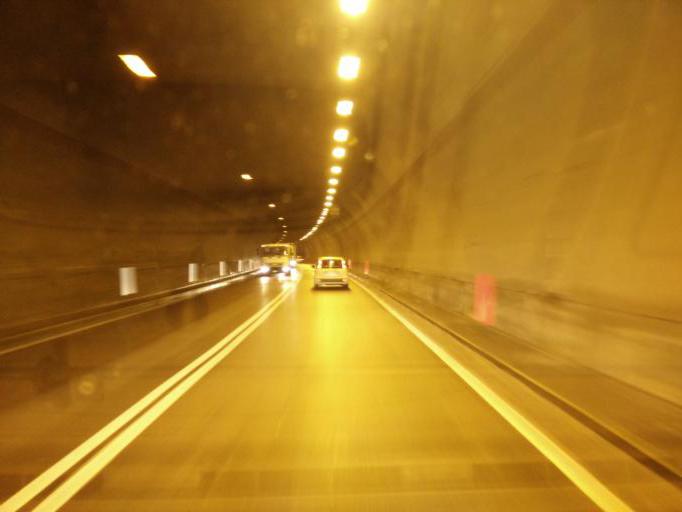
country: IT
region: Tuscany
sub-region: Provincia di Lucca
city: Valdottavo
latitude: 43.9112
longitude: 10.5246
